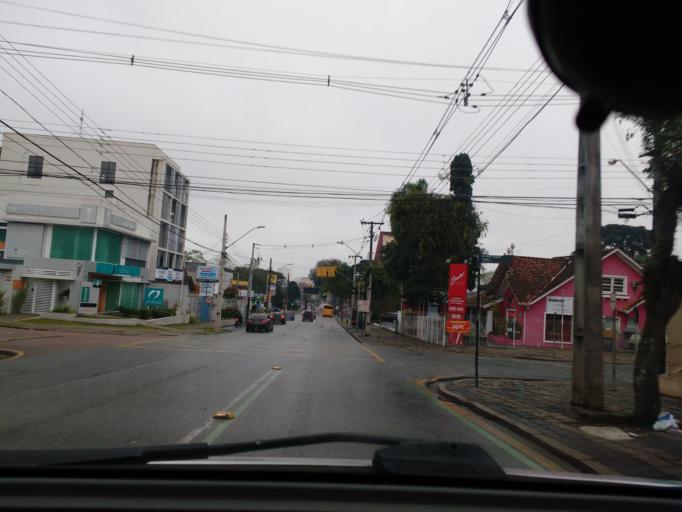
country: BR
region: Parana
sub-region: Curitiba
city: Curitiba
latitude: -25.4276
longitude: -49.2434
